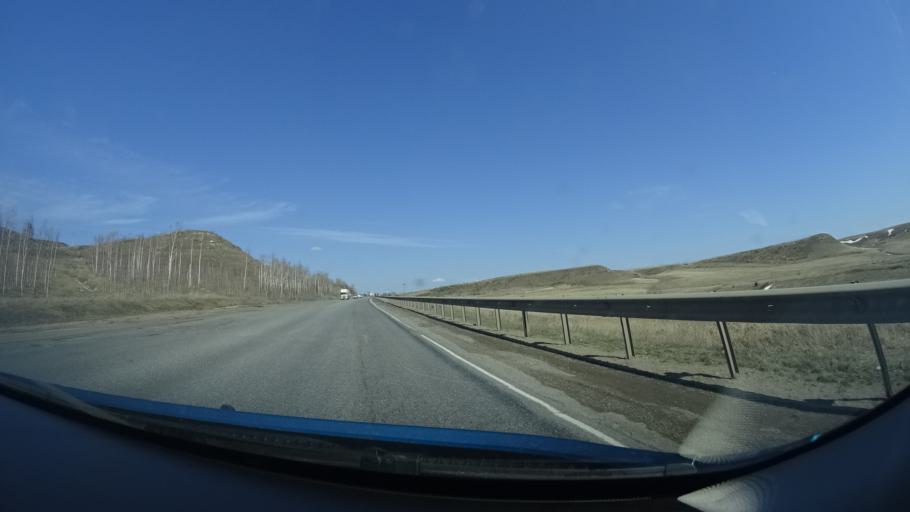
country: RU
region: Bashkortostan
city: Subkhankulovo
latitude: 54.4953
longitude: 53.9373
